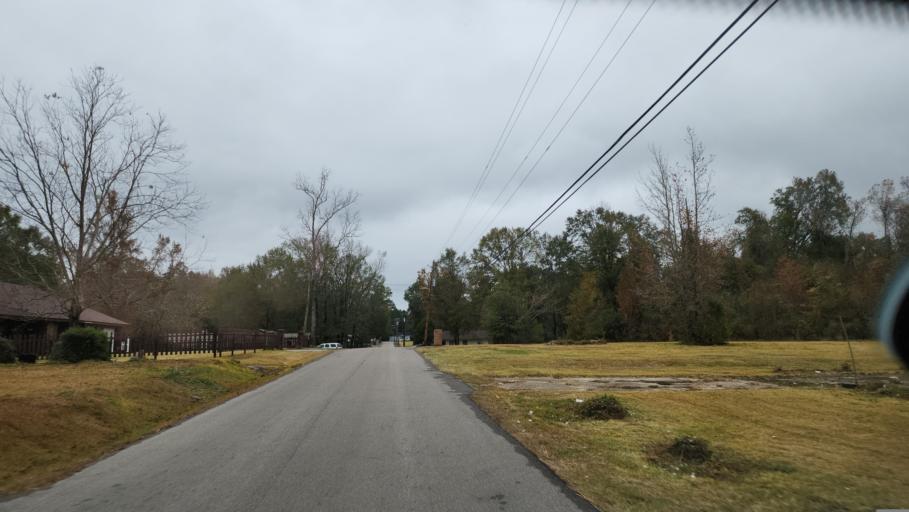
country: US
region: Mississippi
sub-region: Forrest County
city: Hattiesburg
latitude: 31.3000
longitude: -89.3013
